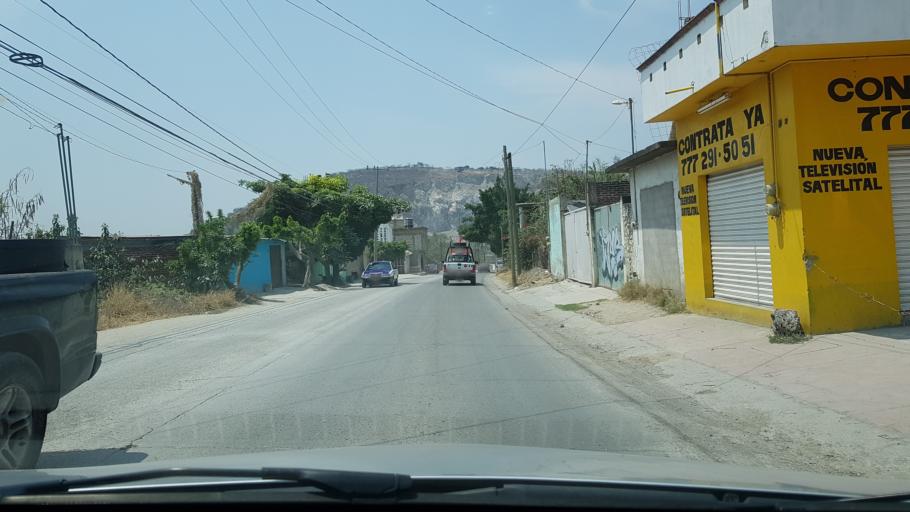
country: MX
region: Morelos
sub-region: Jiutepec
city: Calera Chica
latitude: 18.8619
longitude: -99.1764
